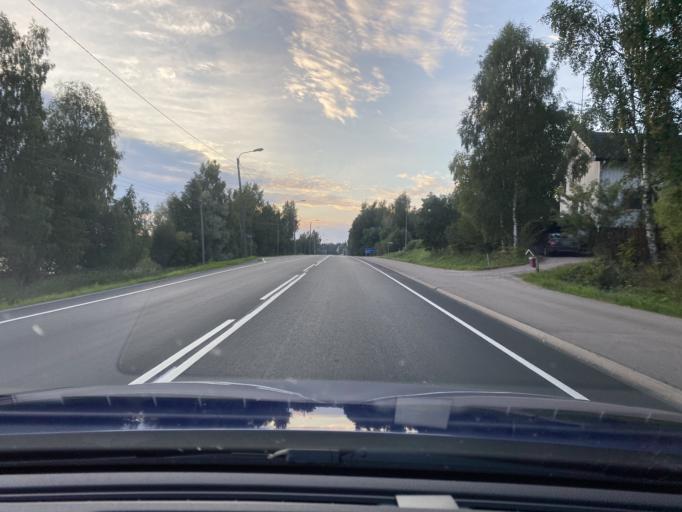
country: FI
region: Satakunta
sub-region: Pohjois-Satakunta
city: Kankaanpaeae
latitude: 61.8220
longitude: 22.3642
